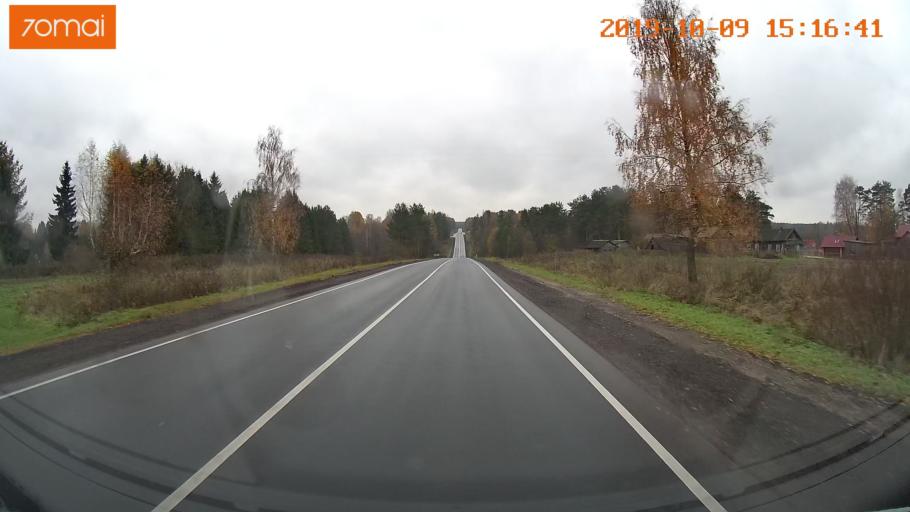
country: RU
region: Kostroma
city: Susanino
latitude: 58.1078
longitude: 41.5853
